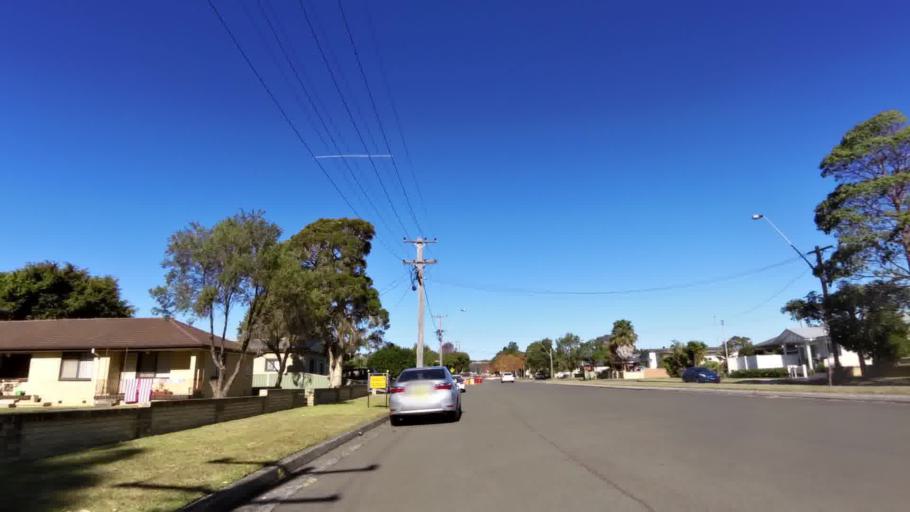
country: AU
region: New South Wales
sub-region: Shellharbour
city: Albion Park Rail
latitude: -34.5573
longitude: 150.8184
